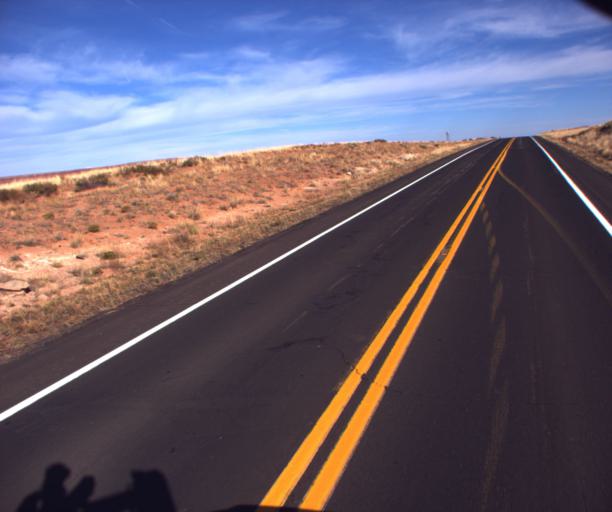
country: US
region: Arizona
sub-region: Apache County
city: Lukachukai
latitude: 36.9616
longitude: -109.4052
